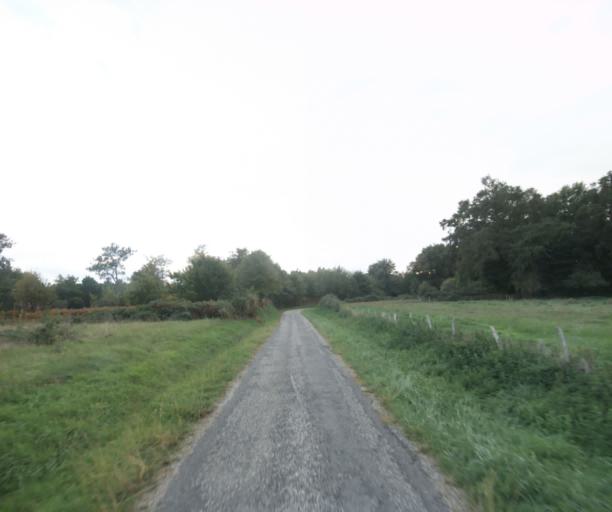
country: FR
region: Midi-Pyrenees
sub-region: Departement du Gers
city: Montreal
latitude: 43.9752
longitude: 0.1115
